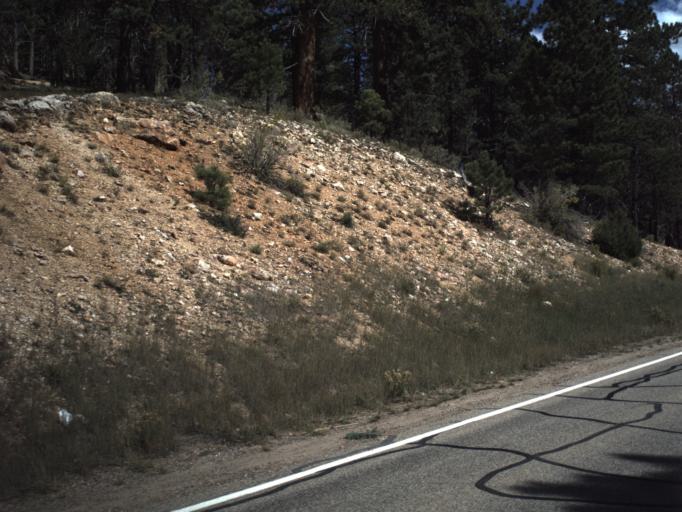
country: US
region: Utah
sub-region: Iron County
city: Parowan
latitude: 37.5224
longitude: -112.6560
